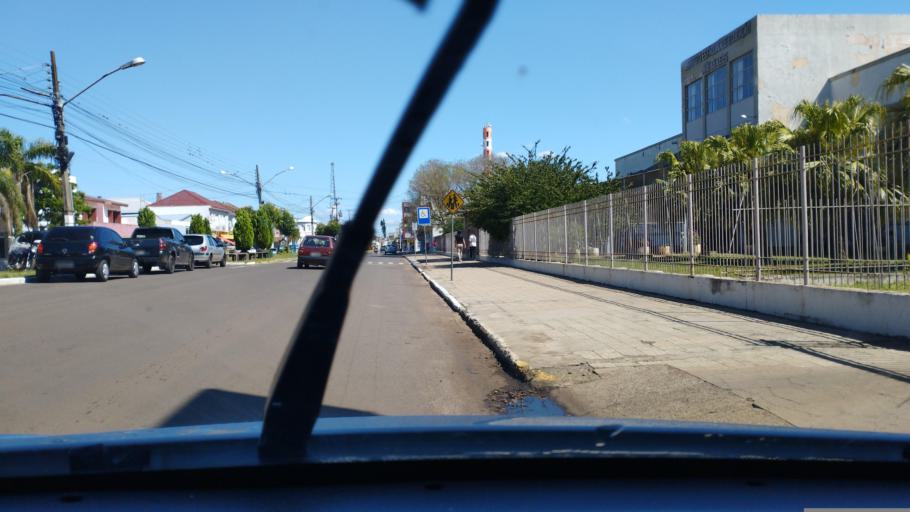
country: BR
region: Rio Grande do Sul
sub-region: Tupancireta
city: Tupancireta
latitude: -29.0784
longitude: -53.8381
